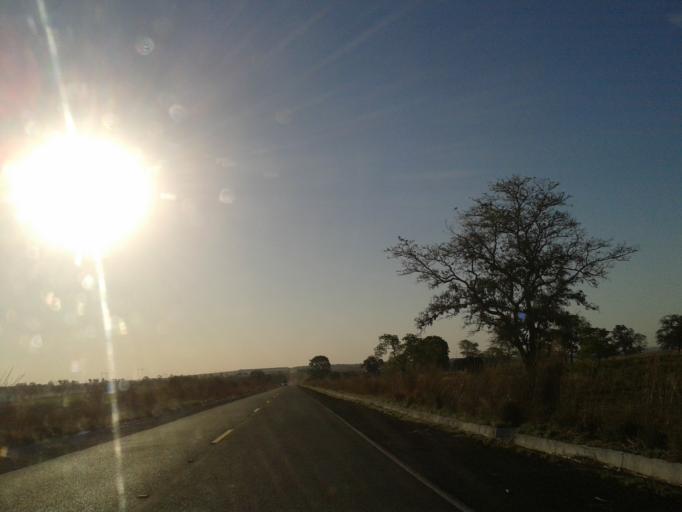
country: BR
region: Minas Gerais
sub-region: Santa Vitoria
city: Santa Vitoria
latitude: -19.0852
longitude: -50.3528
